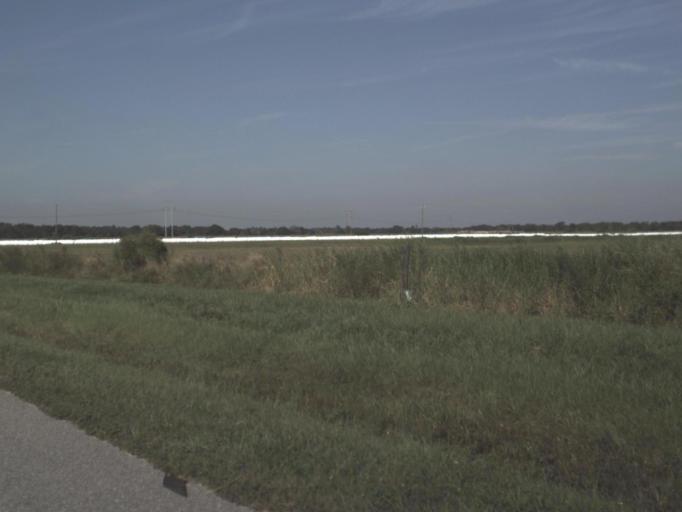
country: US
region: Florida
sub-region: Highlands County
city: Avon Park
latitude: 27.5881
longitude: -81.5935
